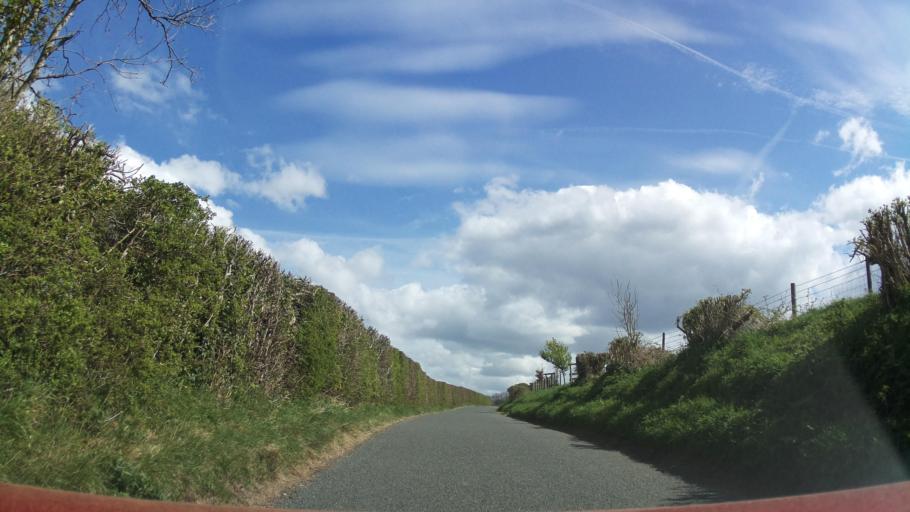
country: GB
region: England
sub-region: West Berkshire
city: Kintbury
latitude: 51.3702
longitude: -1.4819
